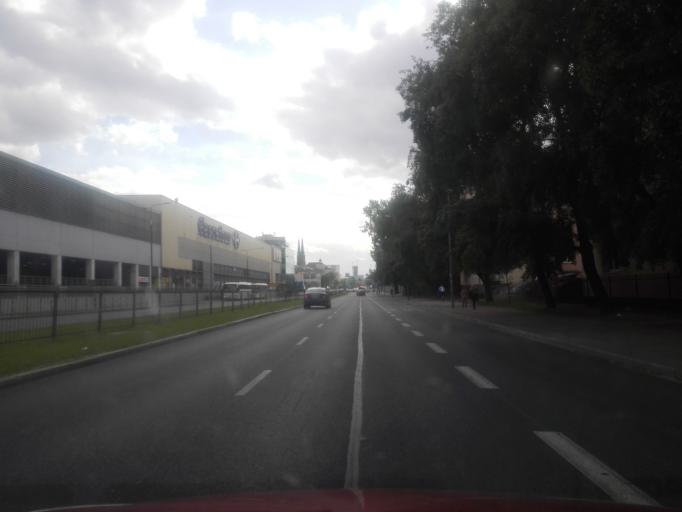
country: PL
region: Masovian Voivodeship
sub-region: Warszawa
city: Praga Polnoc
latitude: 52.2567
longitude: 21.0393
